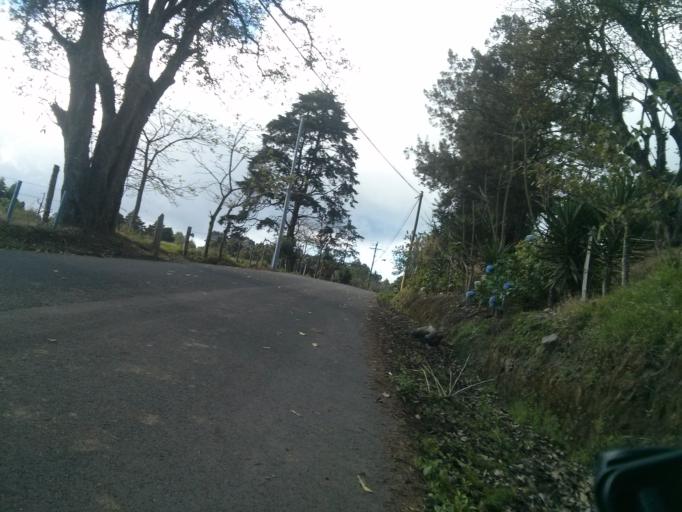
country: CR
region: Cartago
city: Tres Rios
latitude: 9.9194
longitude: -83.9574
